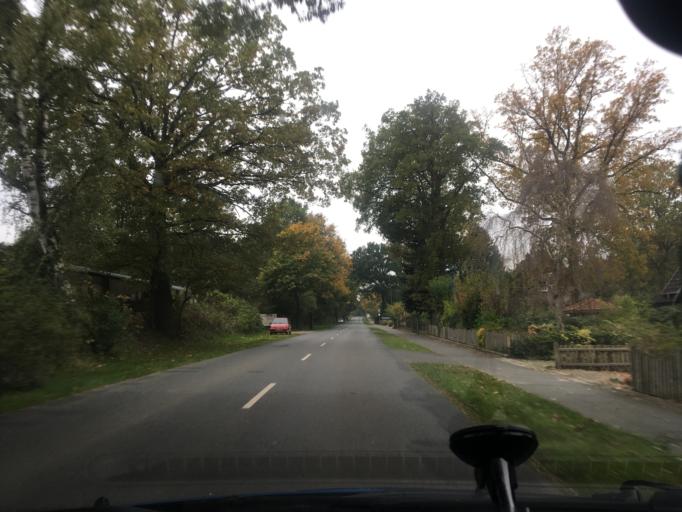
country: DE
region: Lower Saxony
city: Bispingen
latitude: 53.0939
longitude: 10.0215
